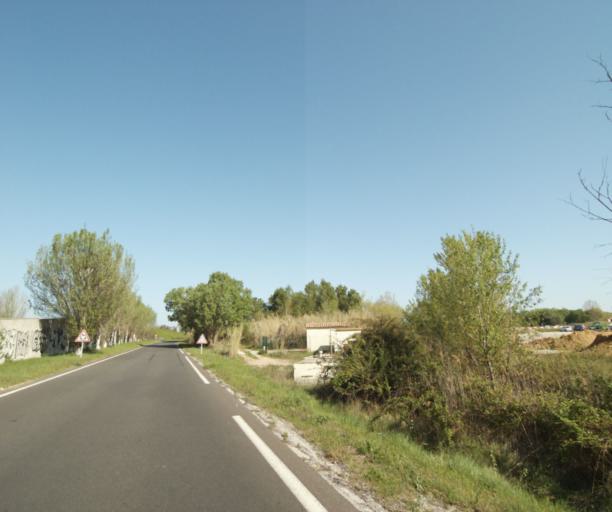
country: FR
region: Languedoc-Roussillon
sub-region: Departement de l'Herault
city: Perols
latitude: 43.5786
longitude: 3.9467
